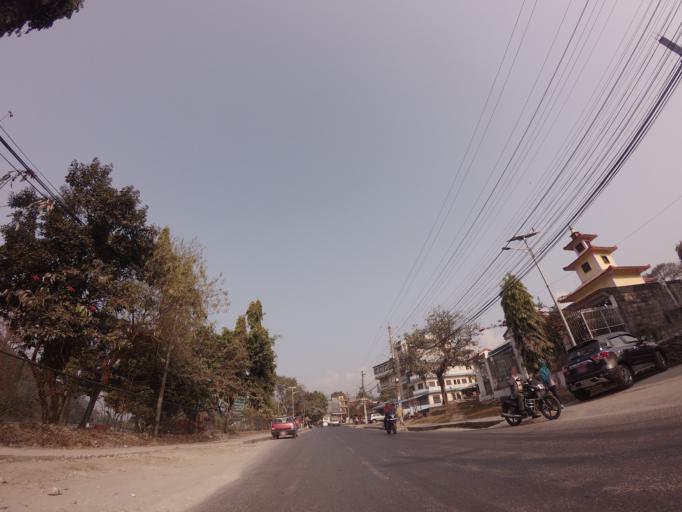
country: NP
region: Western Region
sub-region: Gandaki Zone
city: Pokhara
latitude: 28.1975
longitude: 83.9697
